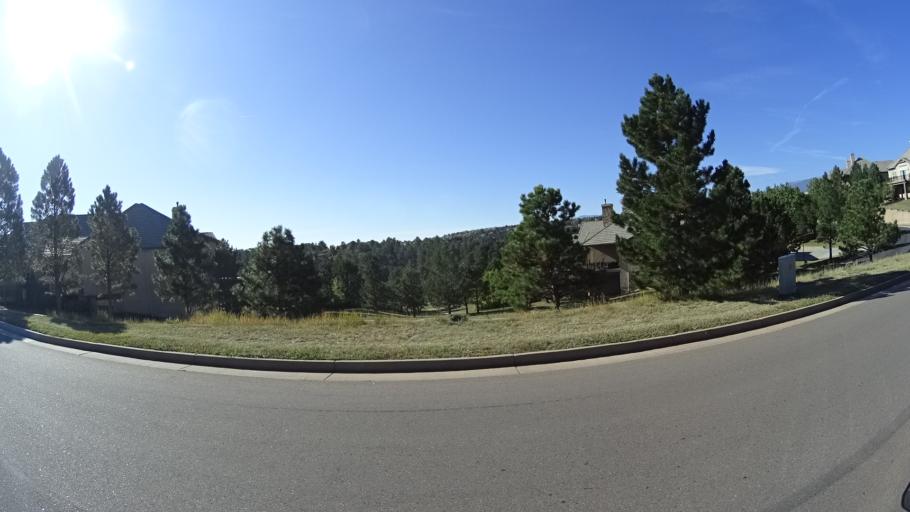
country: US
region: Colorado
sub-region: El Paso County
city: Colorado Springs
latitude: 38.9111
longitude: -104.7919
